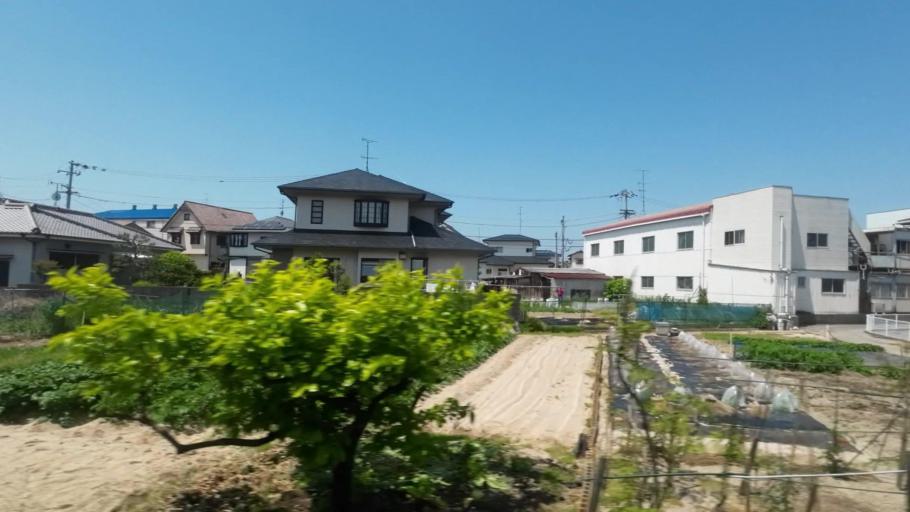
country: JP
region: Ehime
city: Hojo
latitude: 33.9633
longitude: 132.7744
